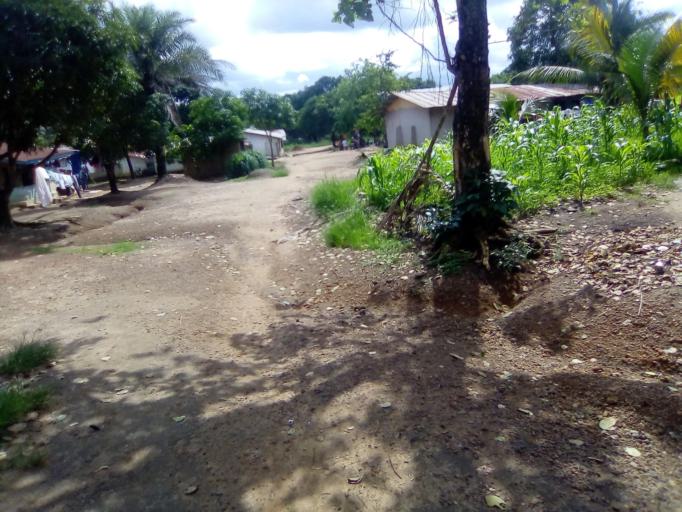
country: SL
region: Southern Province
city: Baoma
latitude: 7.9847
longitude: -11.7231
